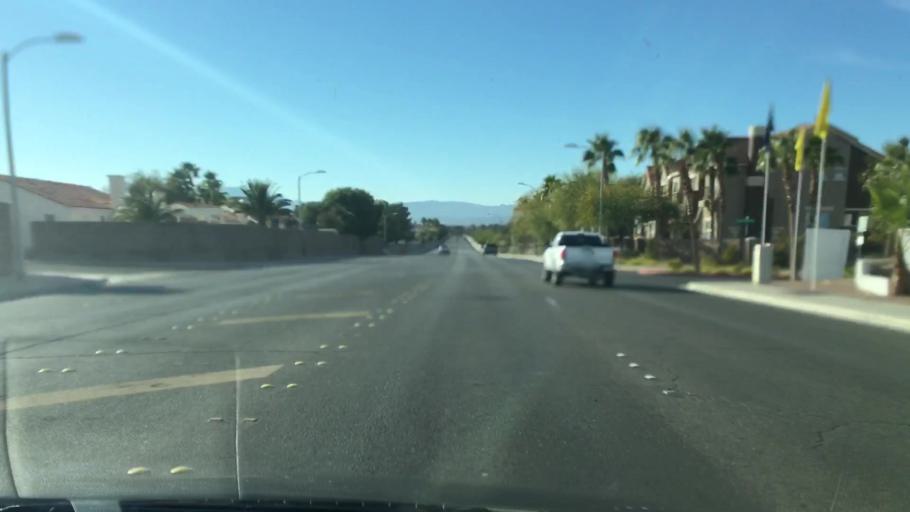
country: US
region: Nevada
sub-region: Clark County
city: Whitney
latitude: 36.0497
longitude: -115.1071
